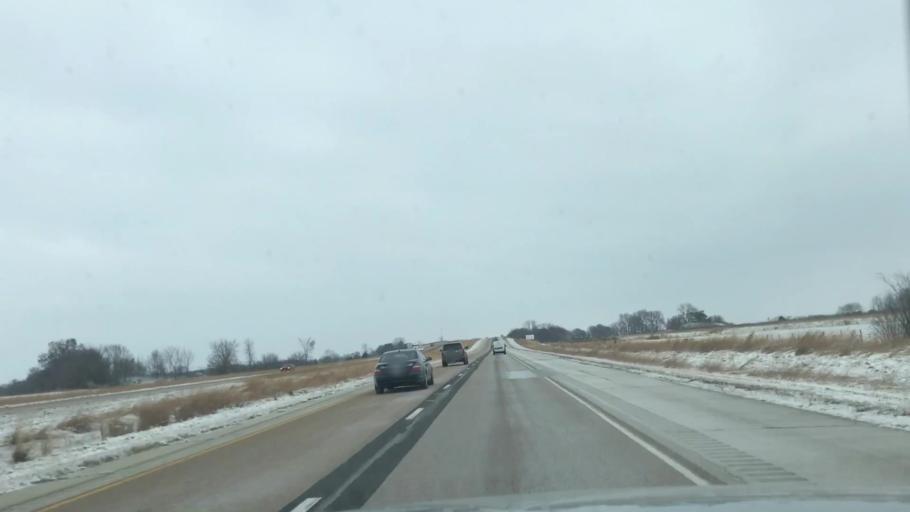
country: US
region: Illinois
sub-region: Montgomery County
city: Litchfield
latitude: 39.2096
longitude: -89.6556
